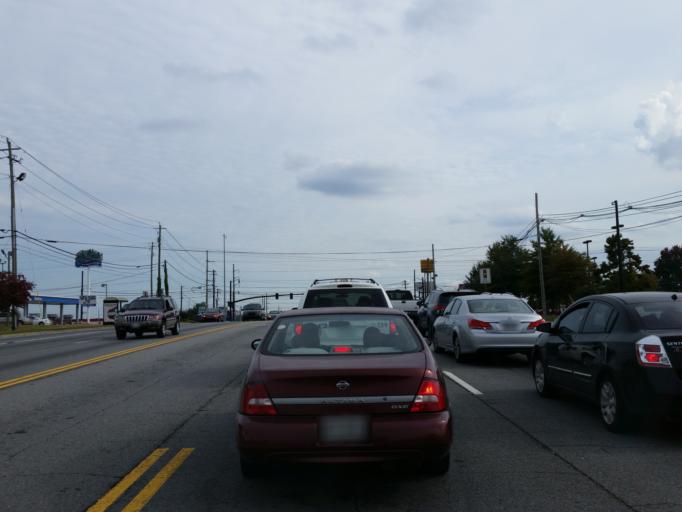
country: US
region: Georgia
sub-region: Cobb County
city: Smyrna
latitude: 33.9040
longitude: -84.4884
